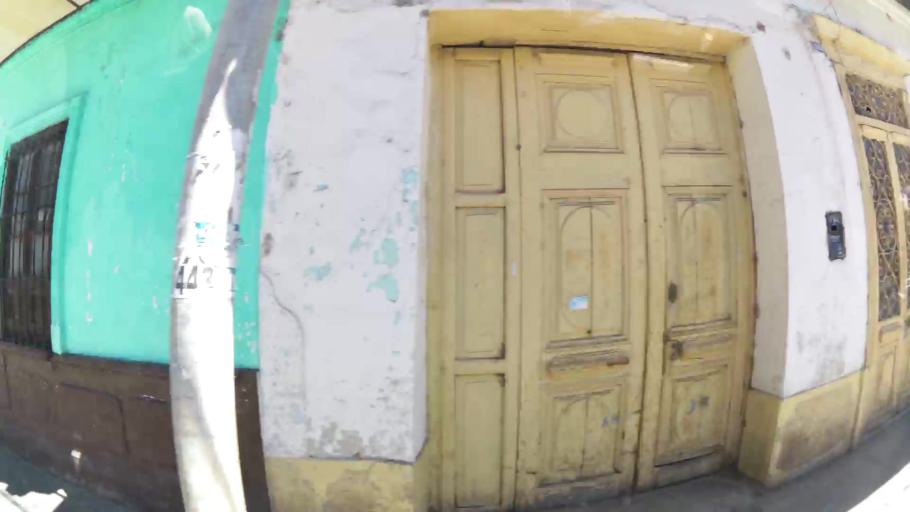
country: PE
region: Junin
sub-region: Provincia de Jauja
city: Jauja
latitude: -11.7743
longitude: -75.4964
